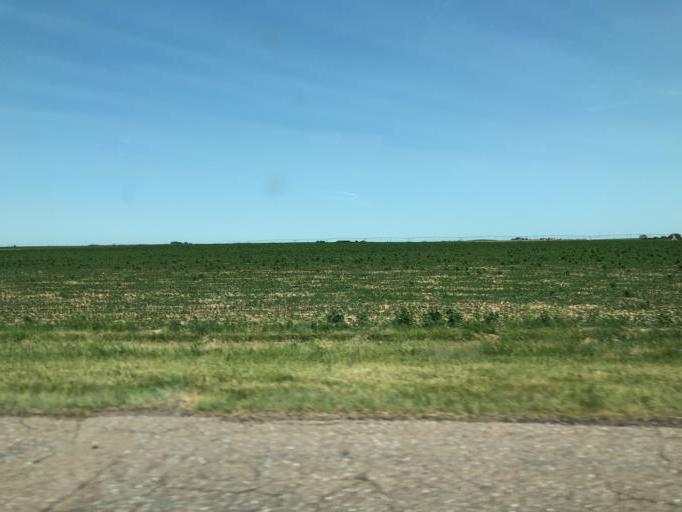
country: US
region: Nebraska
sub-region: Thayer County
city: Hebron
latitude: 40.3120
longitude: -97.5764
